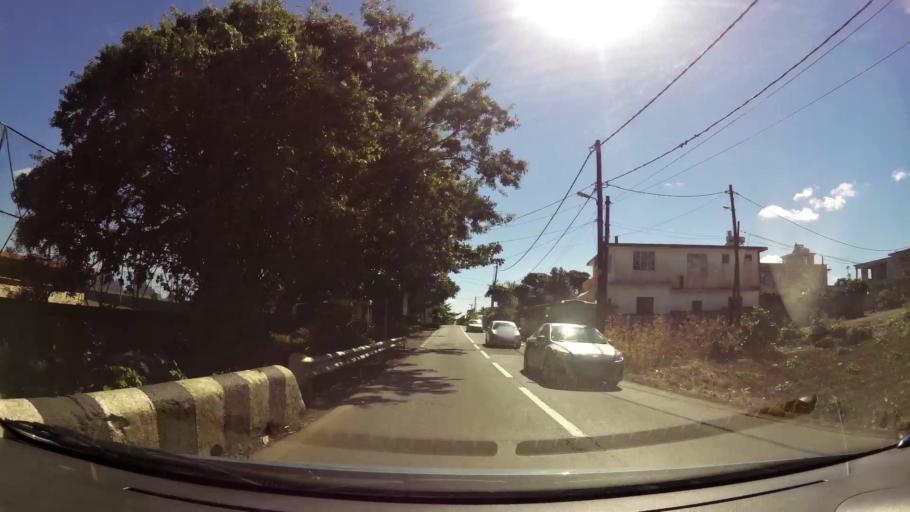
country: MU
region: Plaines Wilhems
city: Curepipe
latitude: -20.3395
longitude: 57.4920
